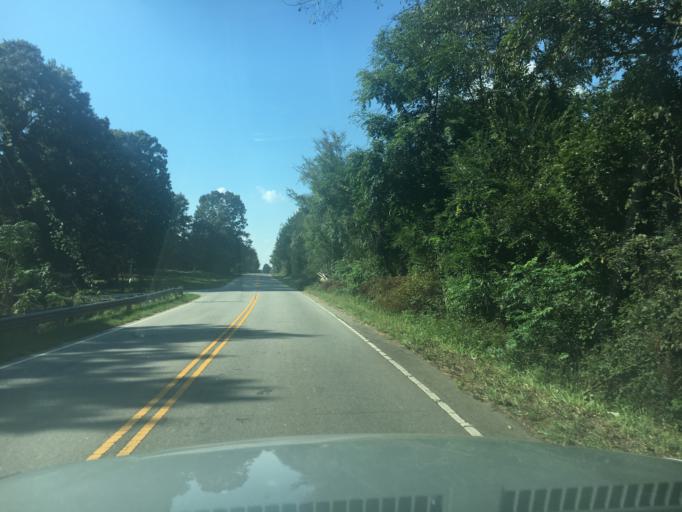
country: US
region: South Carolina
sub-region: Greenville County
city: Fountain Inn
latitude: 34.6215
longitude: -82.2402
